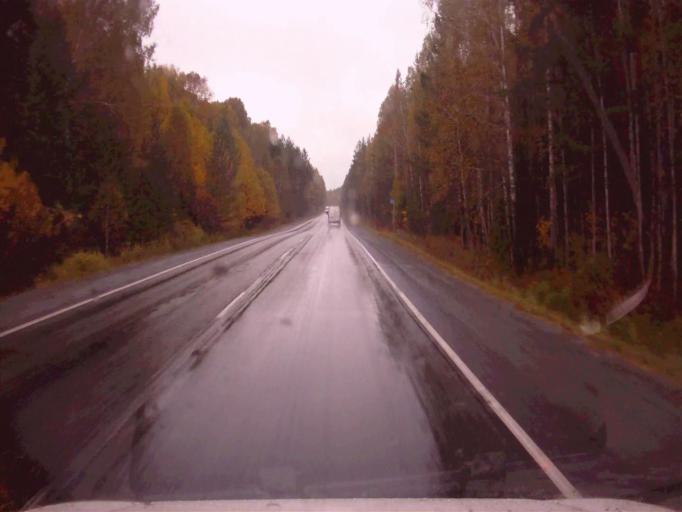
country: RU
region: Chelyabinsk
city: Tayginka
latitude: 55.5618
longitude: 60.6480
